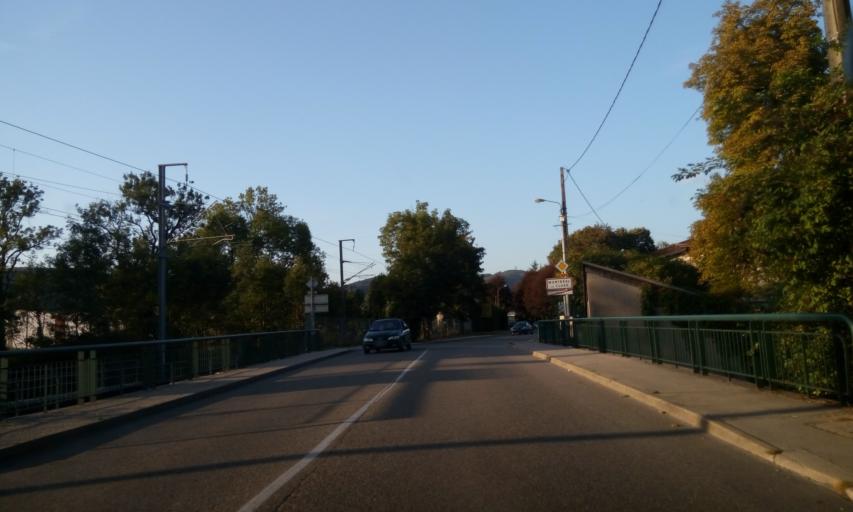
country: FR
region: Rhone-Alpes
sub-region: Departement de l'Ain
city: Montreal-la-Cluse
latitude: 46.1678
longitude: 5.5720
